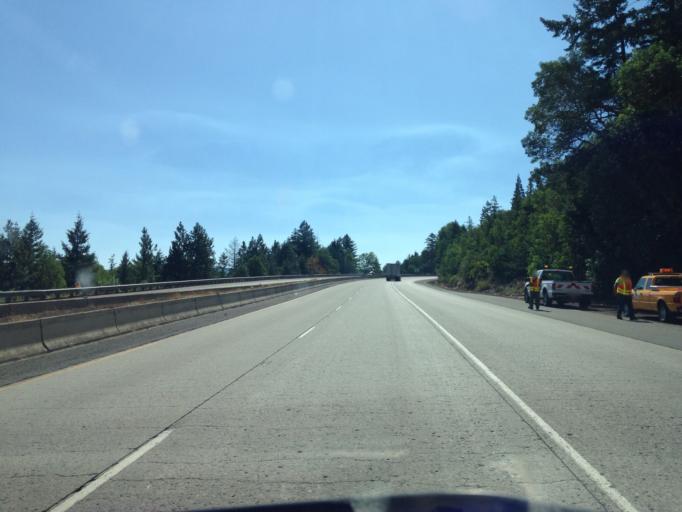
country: US
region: Oregon
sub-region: Jackson County
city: Ashland
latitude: 42.1231
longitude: -122.6269
